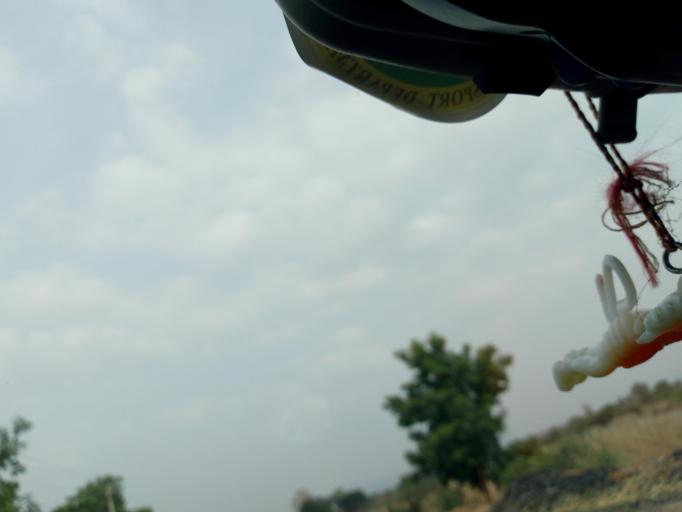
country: IN
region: Andhra Pradesh
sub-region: Prakasam
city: Diguvametta
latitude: 15.3740
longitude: 78.8748
